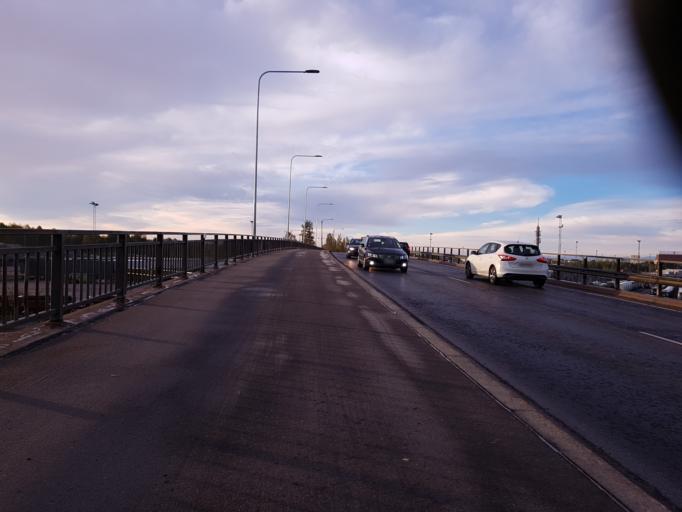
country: FI
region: Uusimaa
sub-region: Helsinki
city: Helsinki
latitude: 60.2182
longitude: 24.9341
